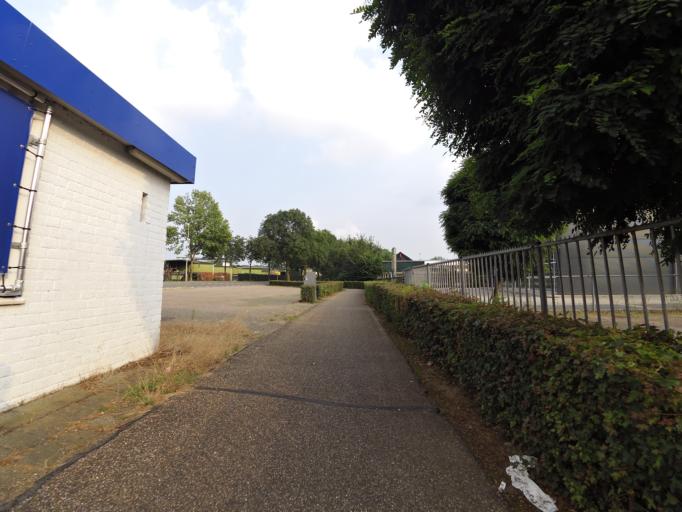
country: NL
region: Gelderland
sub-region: Gemeente Doesburg
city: Doesburg
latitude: 52.0025
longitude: 6.1374
